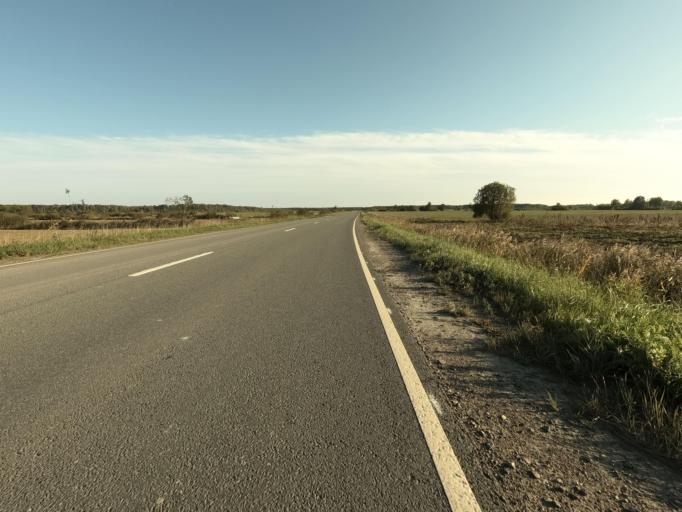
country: RU
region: St.-Petersburg
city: Sapernyy
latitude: 59.7422
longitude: 30.6495
